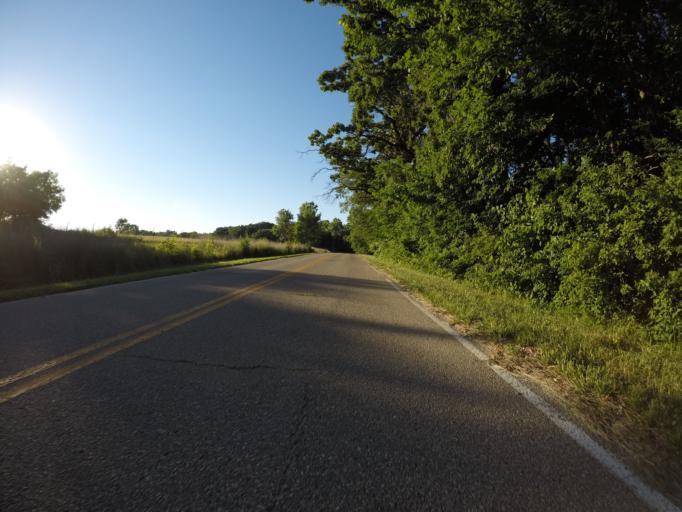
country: US
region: Kansas
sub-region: Riley County
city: Ogden
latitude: 39.1174
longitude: -96.7209
